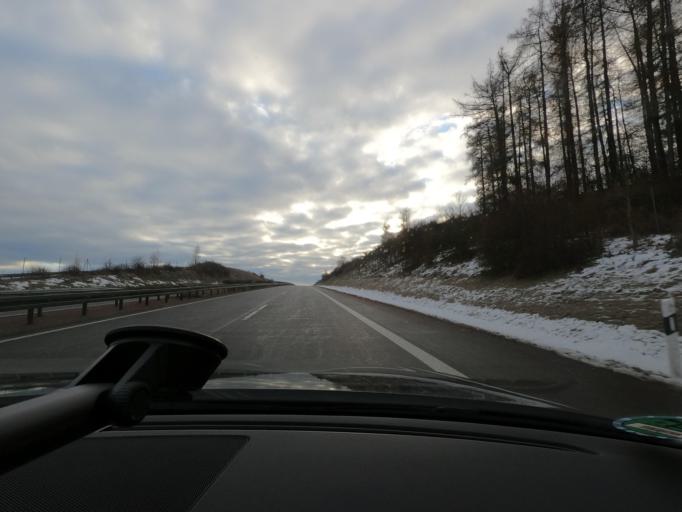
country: DE
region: Thuringia
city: Eisfeld
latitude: 50.4527
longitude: 10.8633
